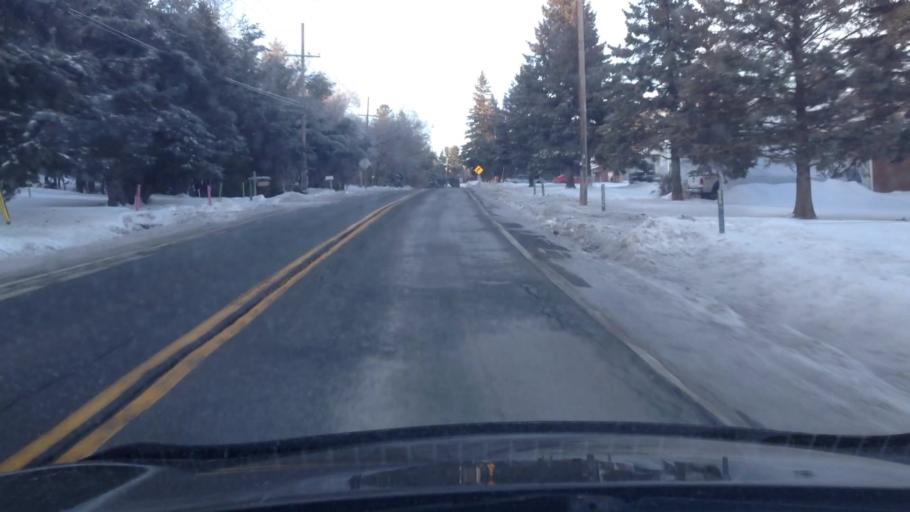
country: CA
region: Quebec
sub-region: Lanaudiere
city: Sainte-Julienne
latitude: 45.9449
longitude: -73.7334
